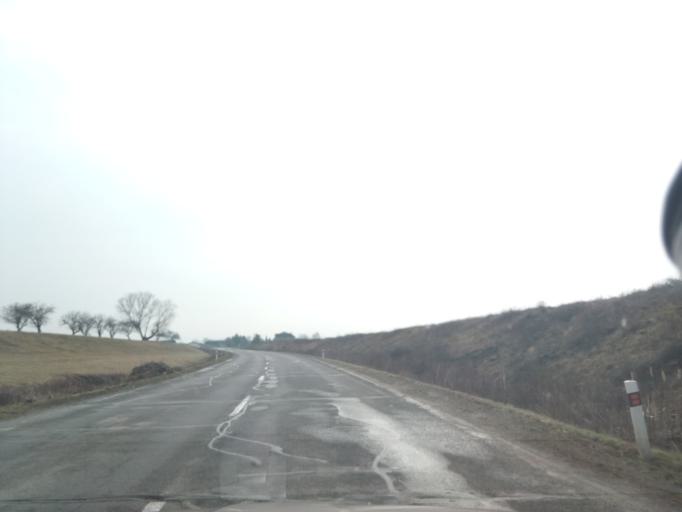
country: SK
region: Kosicky
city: Secovce
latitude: 48.6200
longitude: 21.5937
